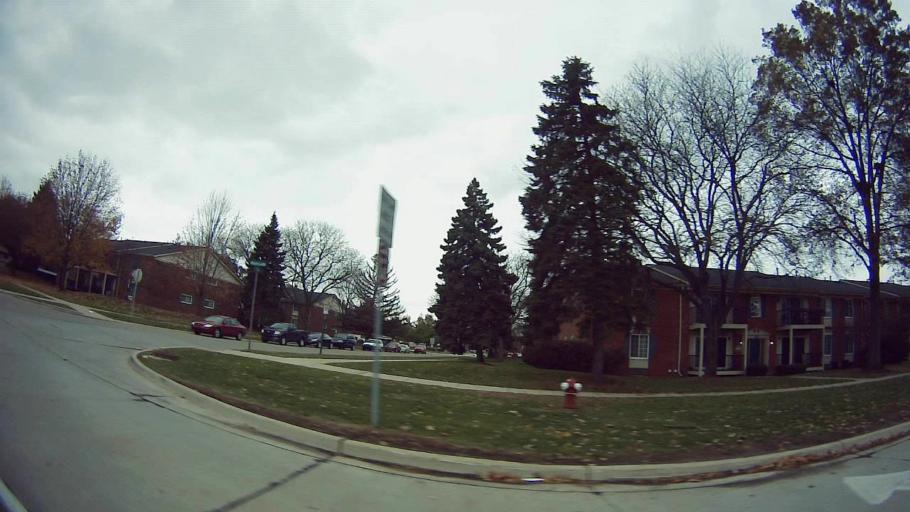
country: US
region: Michigan
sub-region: Macomb County
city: Sterling Heights
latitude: 42.5490
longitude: -83.0045
